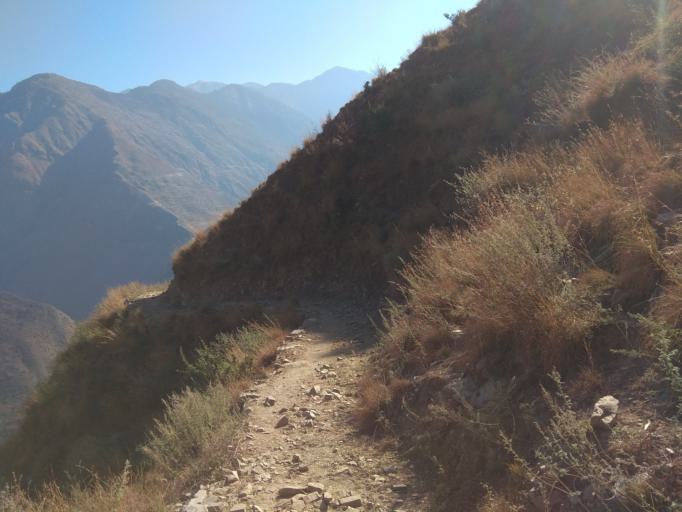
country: NP
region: Mid Western
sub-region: Karnali Zone
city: Jumla
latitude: 29.3154
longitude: 81.7441
